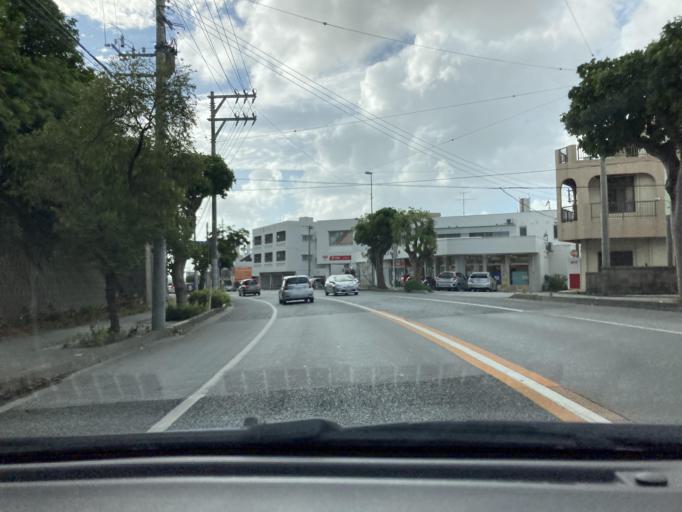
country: JP
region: Okinawa
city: Tomigusuku
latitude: 26.1754
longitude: 127.6852
